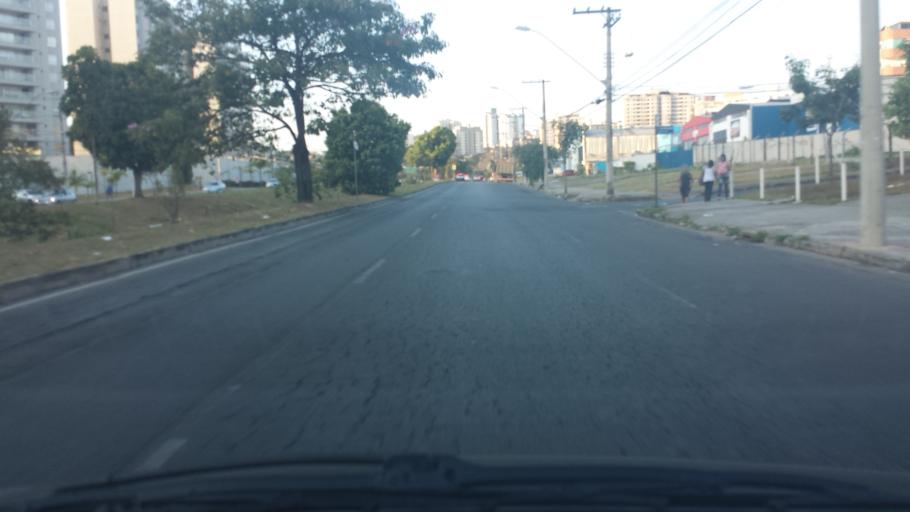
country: BR
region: Minas Gerais
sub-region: Belo Horizonte
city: Belo Horizonte
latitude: -19.8806
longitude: -43.9929
